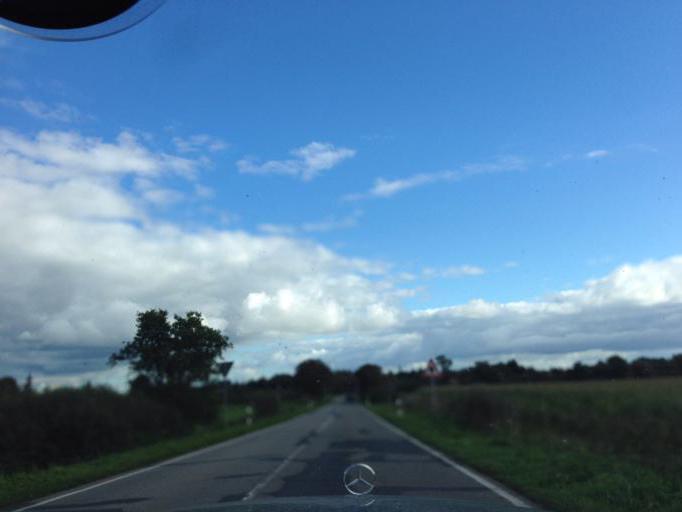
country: DE
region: Schleswig-Holstein
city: Niebull
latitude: 54.7783
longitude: 8.8380
